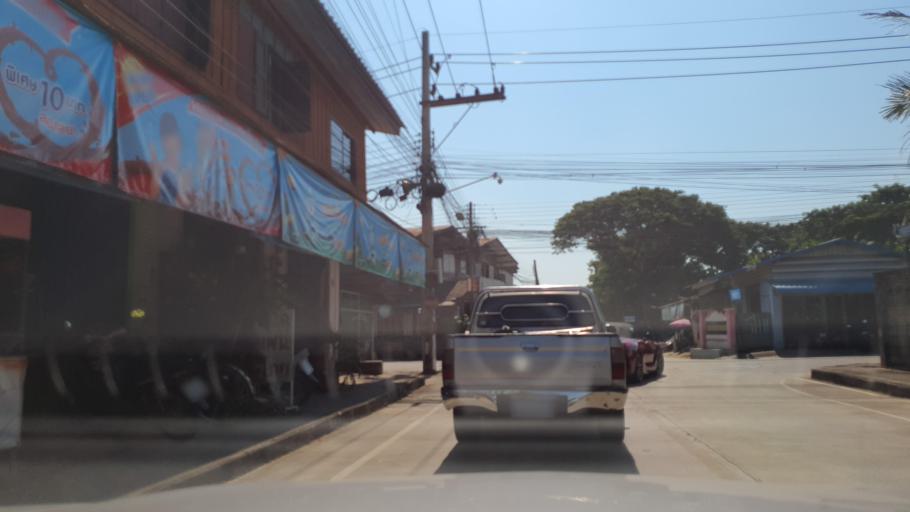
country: TH
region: Nan
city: Nan
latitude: 18.7736
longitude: 100.7680
